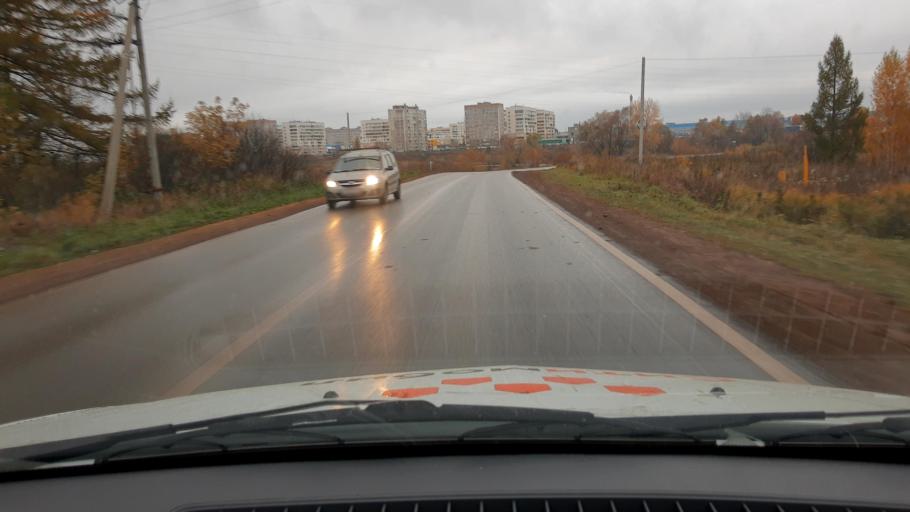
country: RU
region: Bashkortostan
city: Iglino
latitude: 54.7500
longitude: 56.2505
